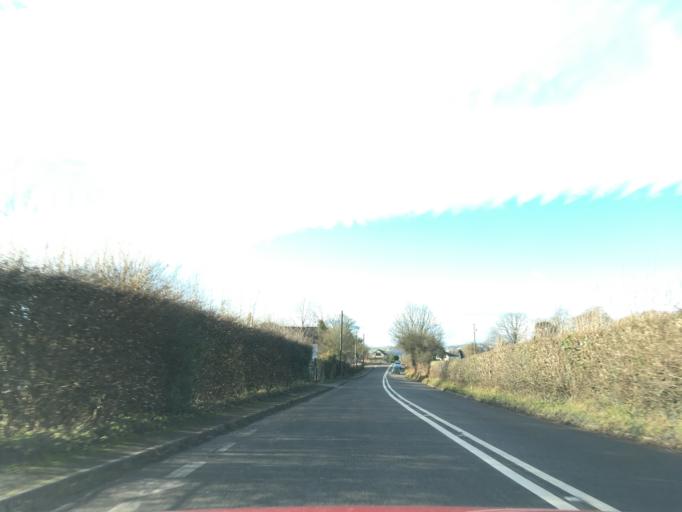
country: GB
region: Wales
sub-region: Monmouthshire
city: Usk
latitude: 51.7186
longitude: -2.9510
